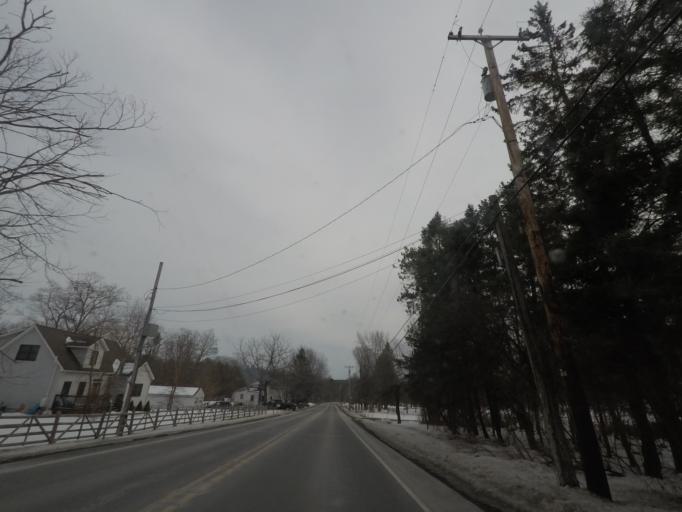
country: US
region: New York
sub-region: Albany County
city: Voorheesville
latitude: 42.5917
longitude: -73.9854
